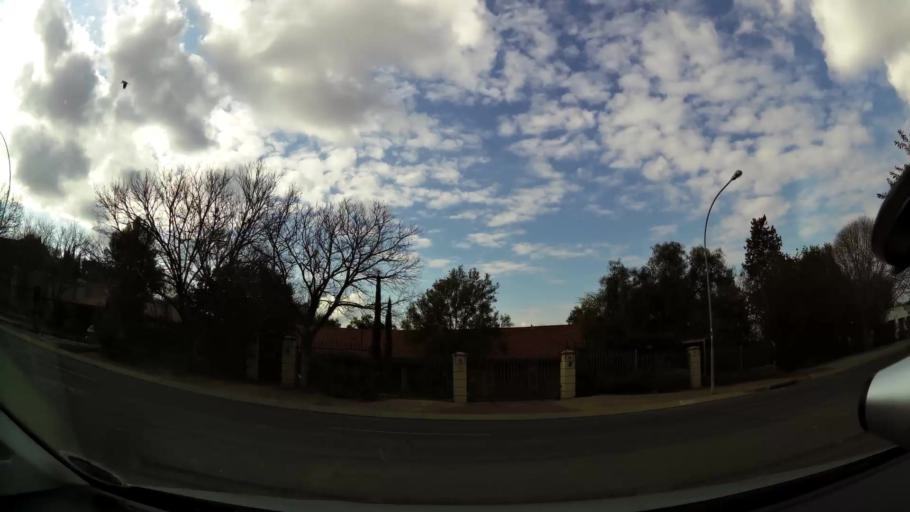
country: ZA
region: Orange Free State
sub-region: Mangaung Metropolitan Municipality
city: Bloemfontein
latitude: -29.0769
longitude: 26.2092
